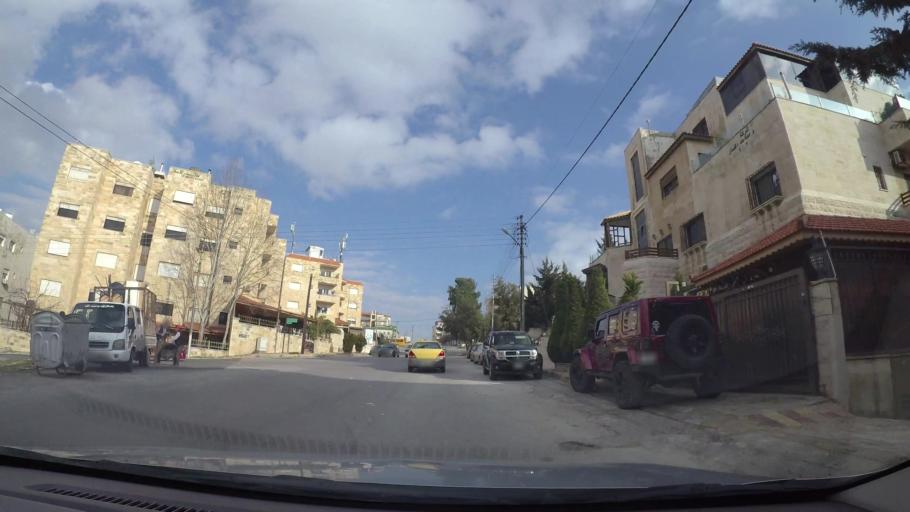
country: JO
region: Amman
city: Wadi as Sir
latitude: 31.9825
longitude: 35.8413
